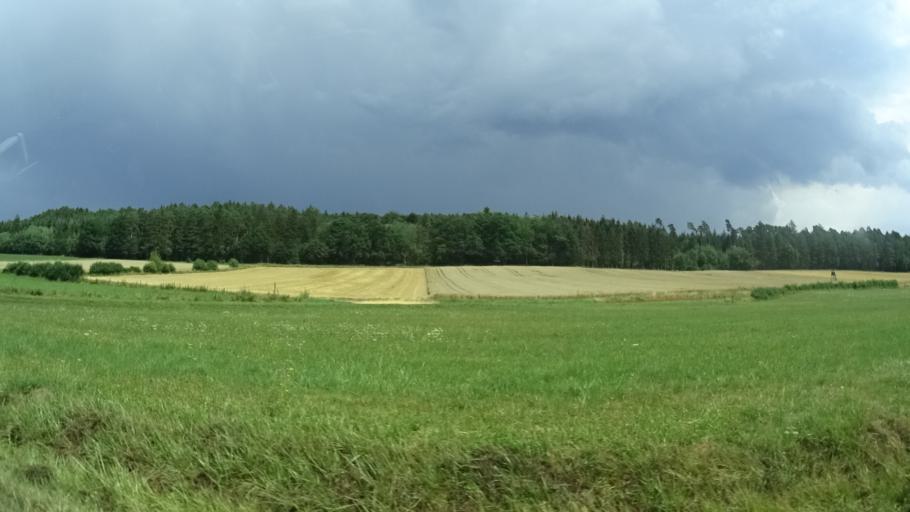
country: DE
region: Hesse
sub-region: Regierungsbezirk Giessen
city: Lauterbach
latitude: 50.6154
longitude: 9.4354
